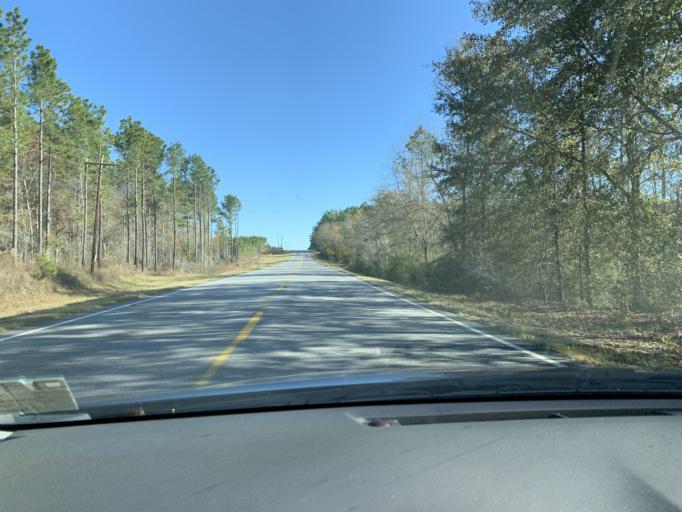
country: US
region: Georgia
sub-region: Ben Hill County
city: Fitzgerald
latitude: 31.7580
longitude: -83.1230
